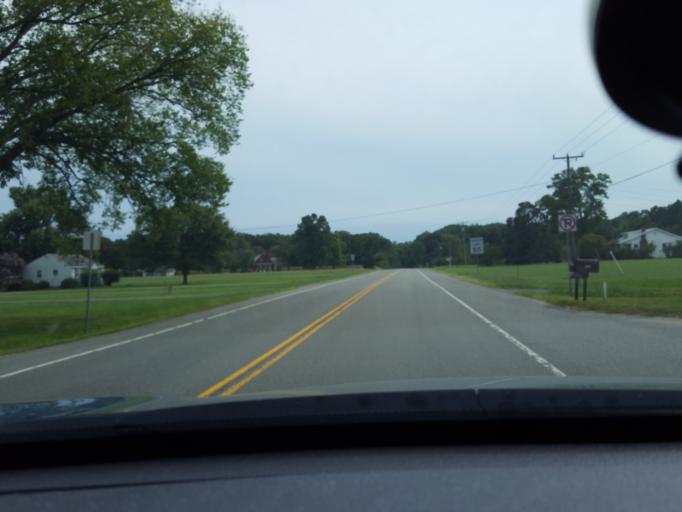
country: US
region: Virginia
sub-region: Hanover County
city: Hanover
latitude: 37.7074
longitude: -77.3837
